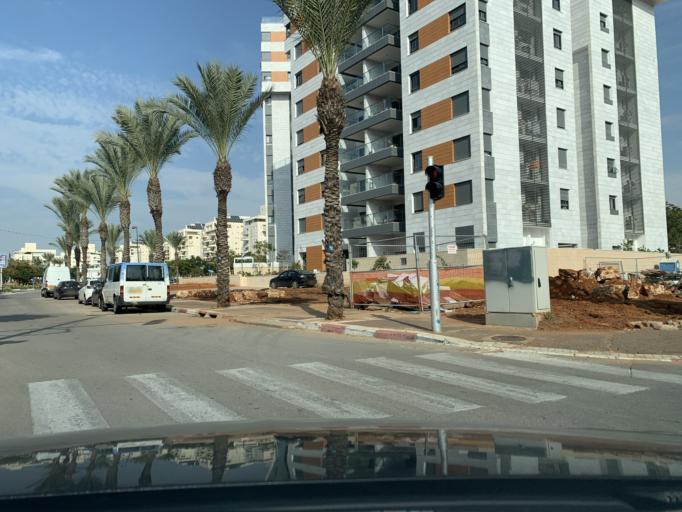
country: IL
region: Central District
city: Ganne Tiqwa
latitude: 32.0536
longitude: 34.8578
